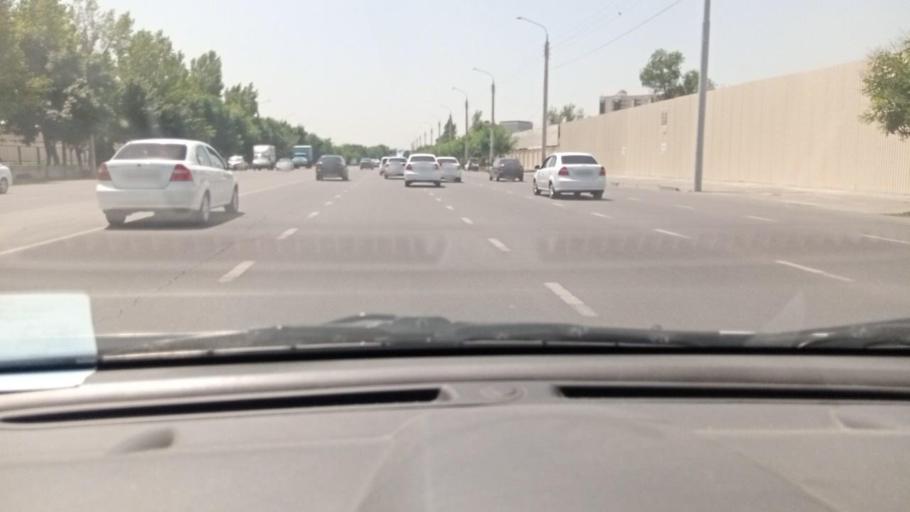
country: UZ
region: Toshkent Shahri
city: Tashkent
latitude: 41.2753
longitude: 69.2702
